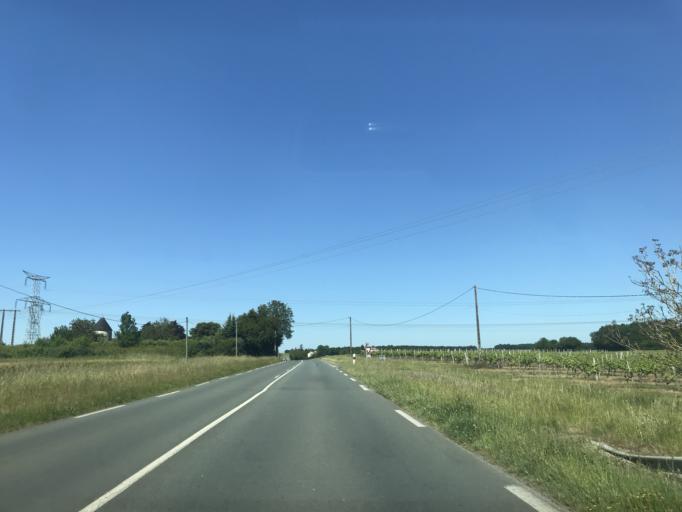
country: FR
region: Poitou-Charentes
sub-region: Departement de la Charente-Maritime
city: Pons
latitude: 45.5720
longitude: -0.6024
